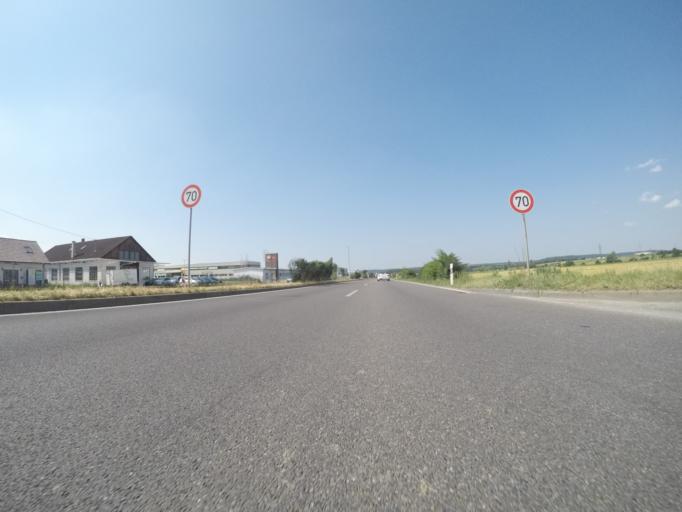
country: DE
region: Baden-Wuerttemberg
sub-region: Regierungsbezirk Stuttgart
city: Dettingen unter Teck
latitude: 48.6212
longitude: 9.4554
